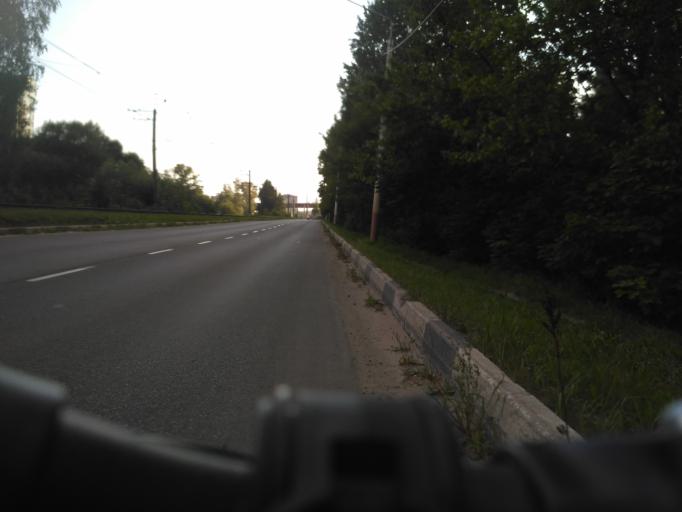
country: RU
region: Moskovskaya
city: Dubna
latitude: 56.7419
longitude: 37.1659
